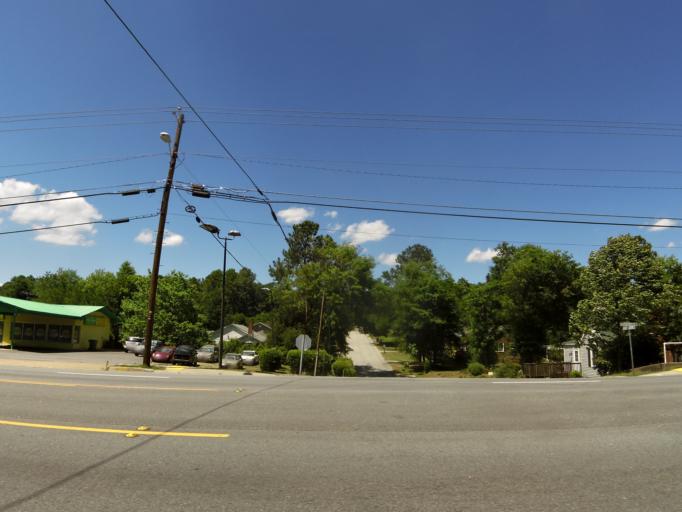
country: US
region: South Carolina
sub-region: Aiken County
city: Aiken
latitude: 33.5655
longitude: -81.7389
